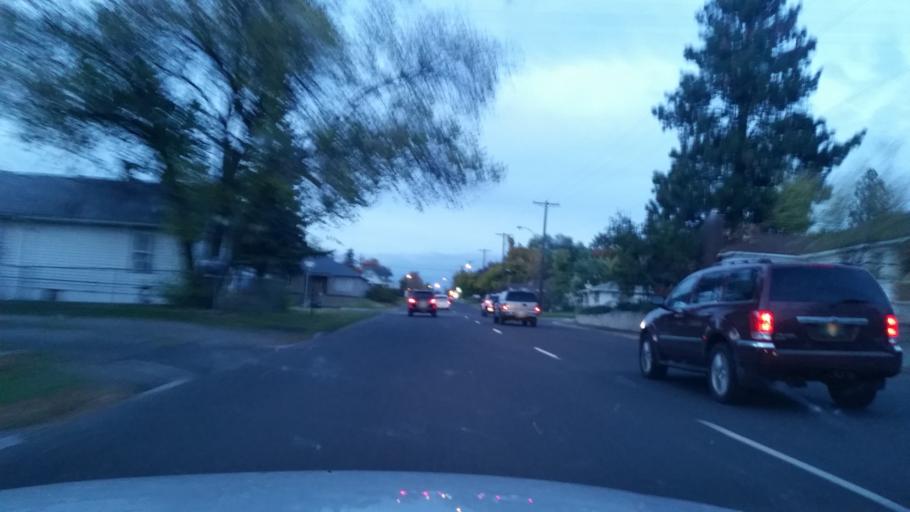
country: US
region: Washington
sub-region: Spokane County
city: Spokane
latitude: 47.6905
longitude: -117.4351
